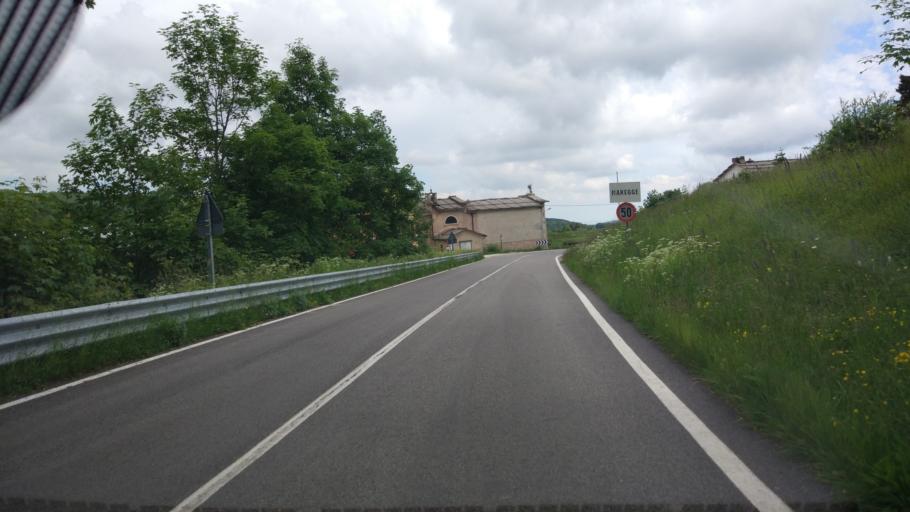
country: IT
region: Veneto
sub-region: Provincia di Verona
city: Bosco Chiesanuova
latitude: 45.6546
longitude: 11.0522
